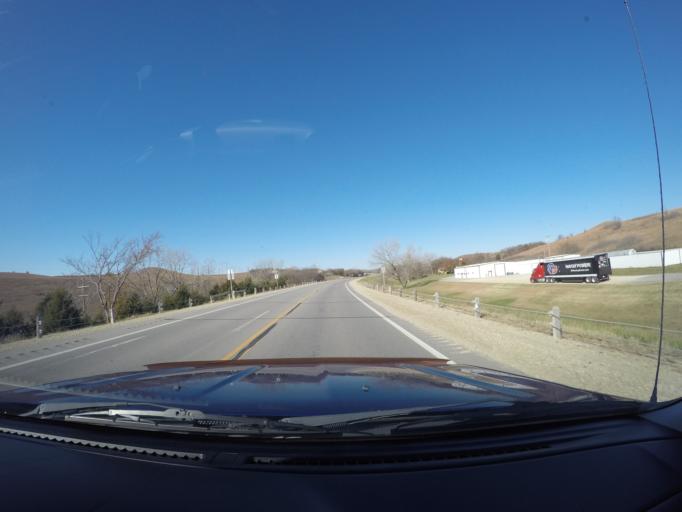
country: US
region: Kansas
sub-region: Riley County
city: Manhattan
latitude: 39.2474
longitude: -96.6278
